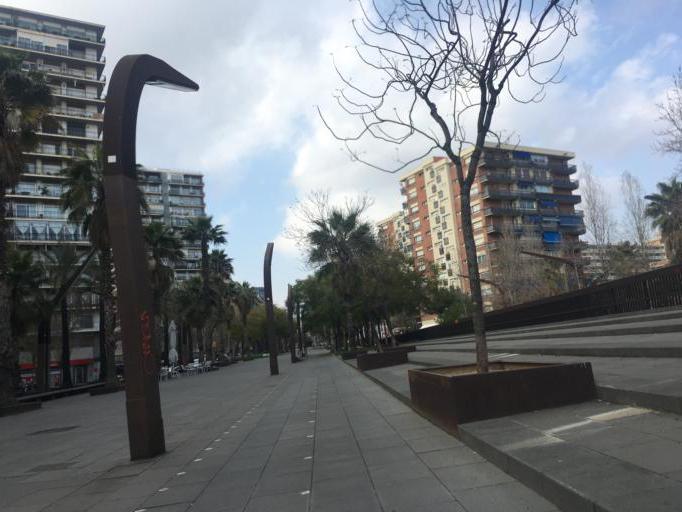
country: ES
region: Catalonia
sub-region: Provincia de Barcelona
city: les Corts
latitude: 41.3805
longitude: 2.1287
